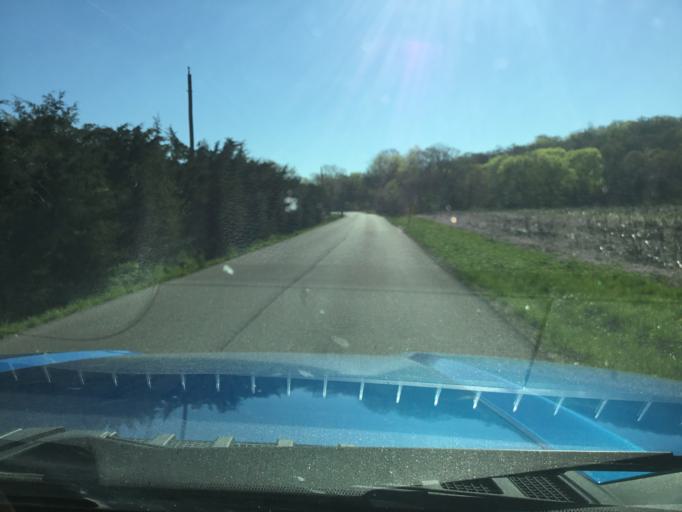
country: US
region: Kansas
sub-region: Douglas County
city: Lawrence
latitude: 38.9933
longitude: -95.3127
